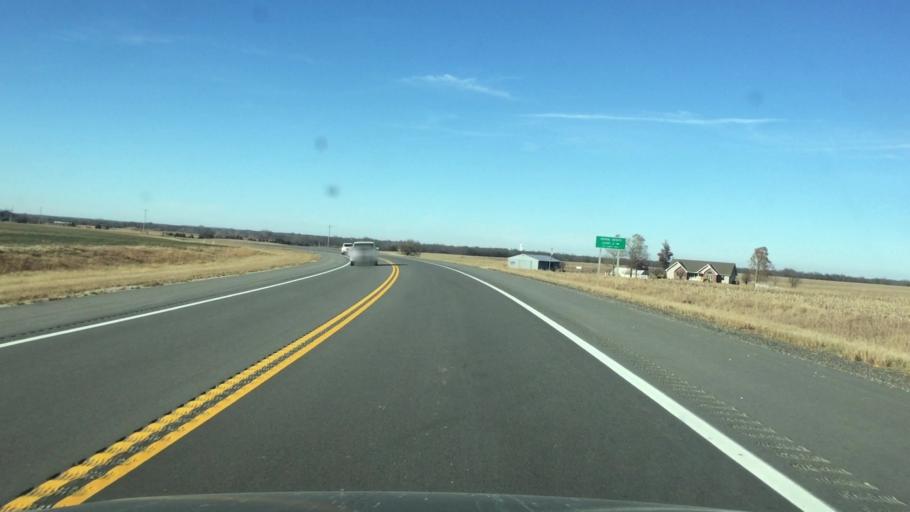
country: US
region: Kansas
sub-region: Franklin County
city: Ottawa
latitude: 38.4607
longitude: -95.2504
